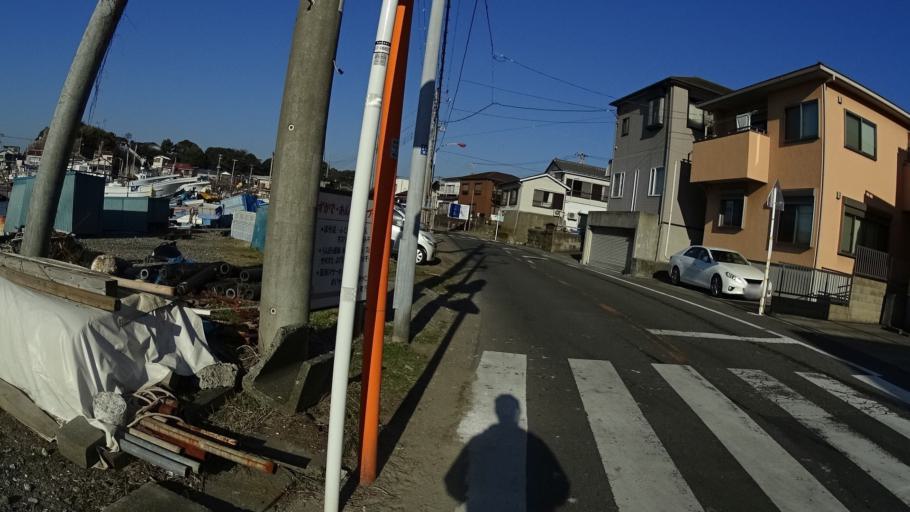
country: JP
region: Kanagawa
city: Miura
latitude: 35.1986
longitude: 139.6063
